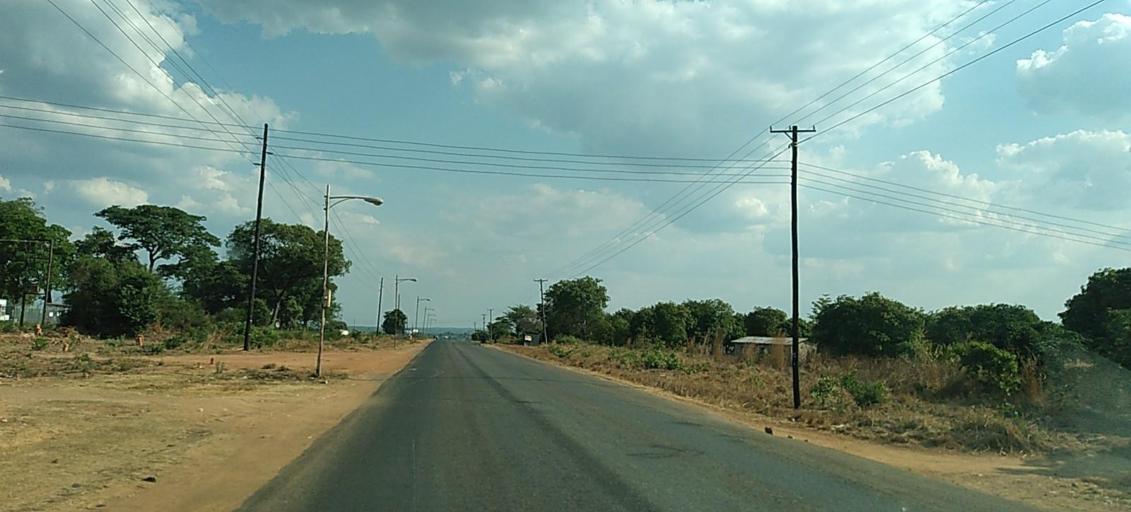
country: ZM
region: Copperbelt
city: Luanshya
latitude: -13.3235
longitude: 28.4152
